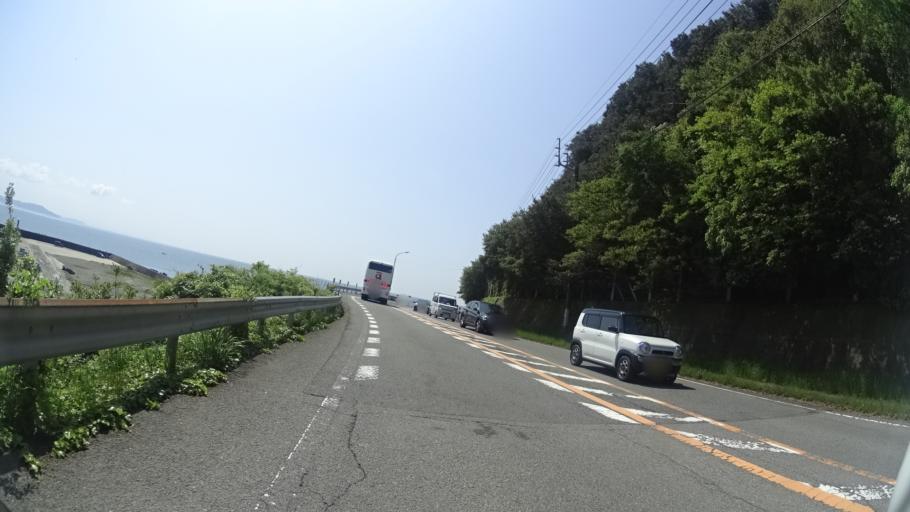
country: JP
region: Tokushima
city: Narutocho-mitsuishi
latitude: 34.2144
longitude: 134.6296
